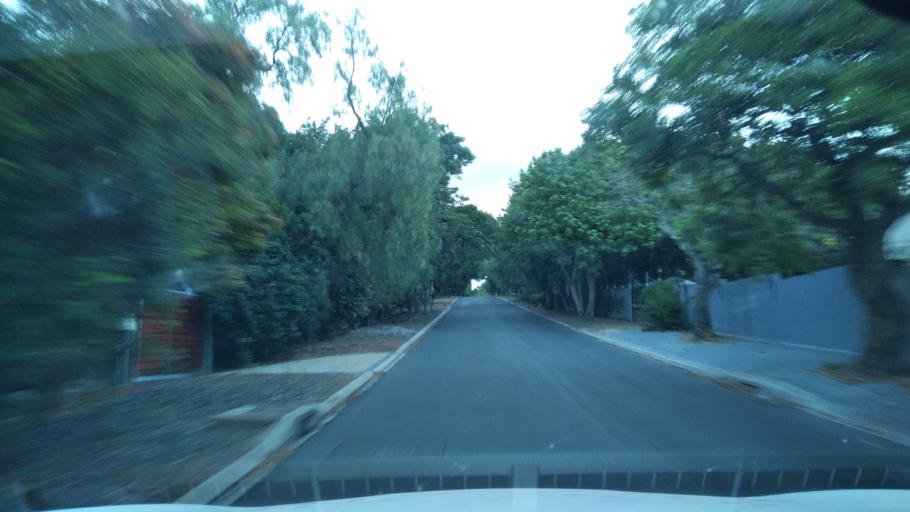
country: ZA
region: Western Cape
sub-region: City of Cape Town
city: Kraaifontein
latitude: -33.8201
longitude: 18.6609
